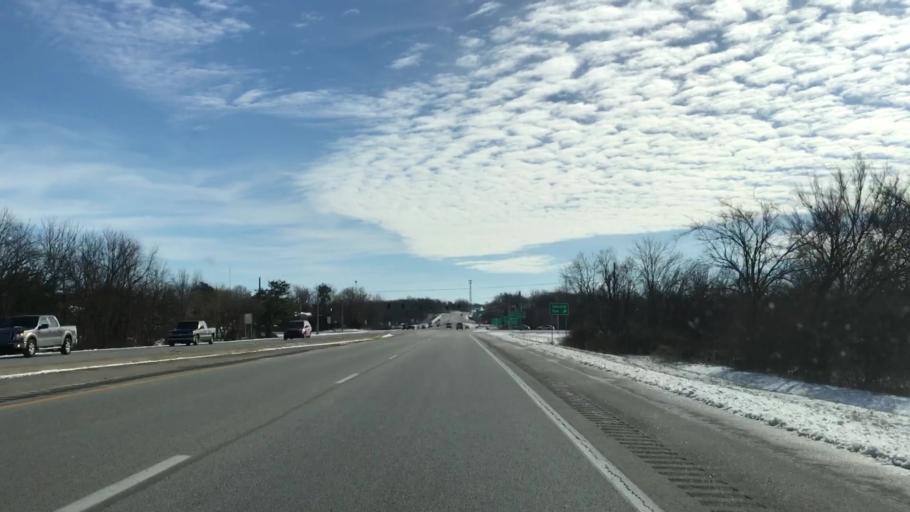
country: US
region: Kentucky
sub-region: Hardin County
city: Elizabethtown
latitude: 37.6933
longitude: -85.8741
